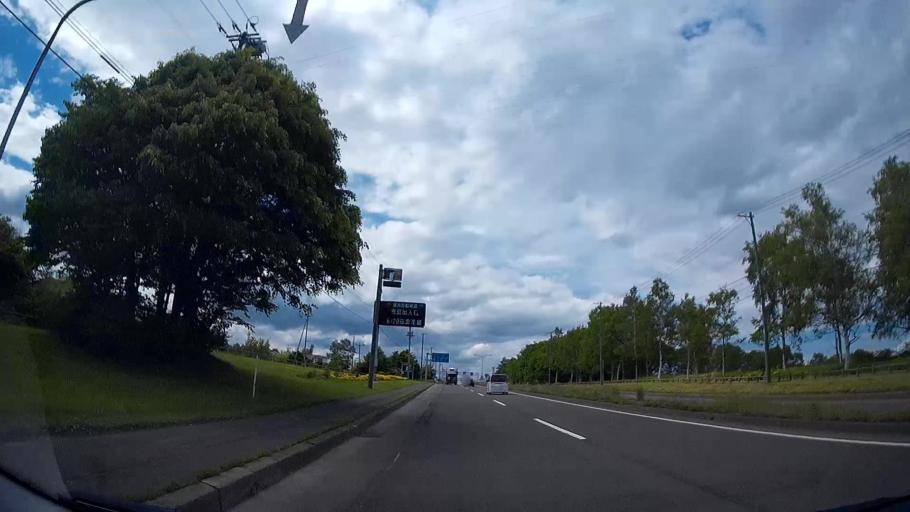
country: JP
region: Hokkaido
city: Chitose
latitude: 42.8588
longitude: 141.6033
